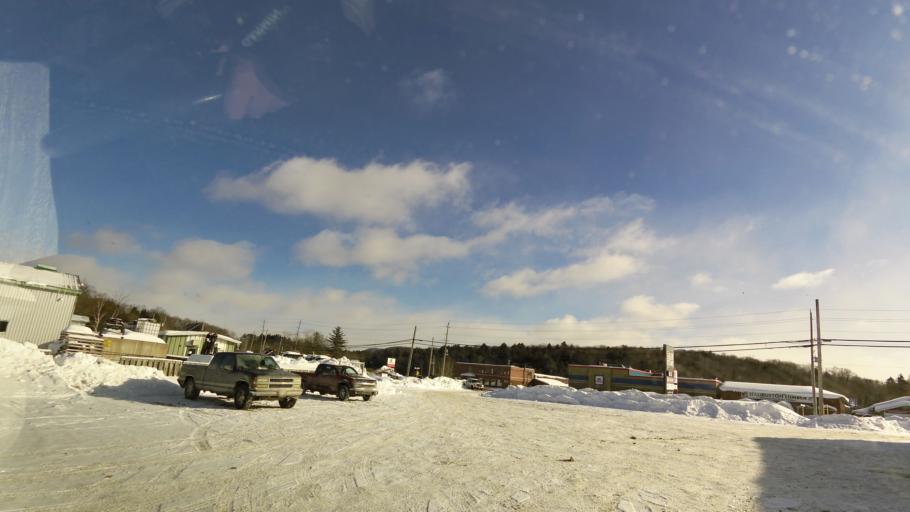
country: CA
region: Ontario
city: Bancroft
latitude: 45.0468
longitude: -78.5342
